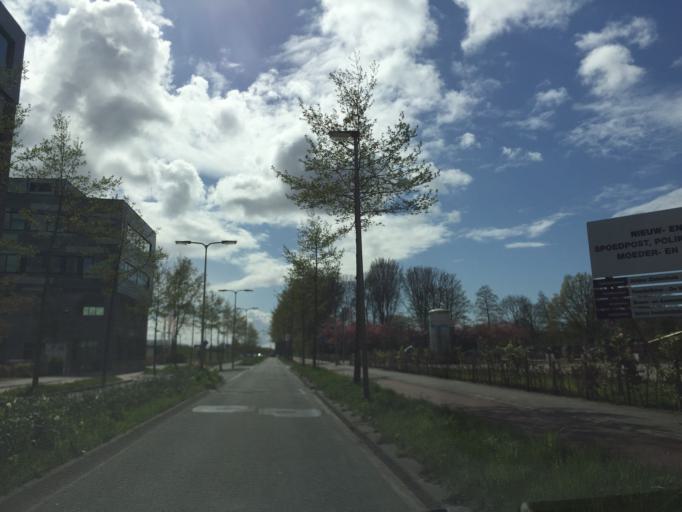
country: NL
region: South Holland
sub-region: Gemeente Leiderdorp
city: Leiderdorp
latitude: 52.1559
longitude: 4.5421
